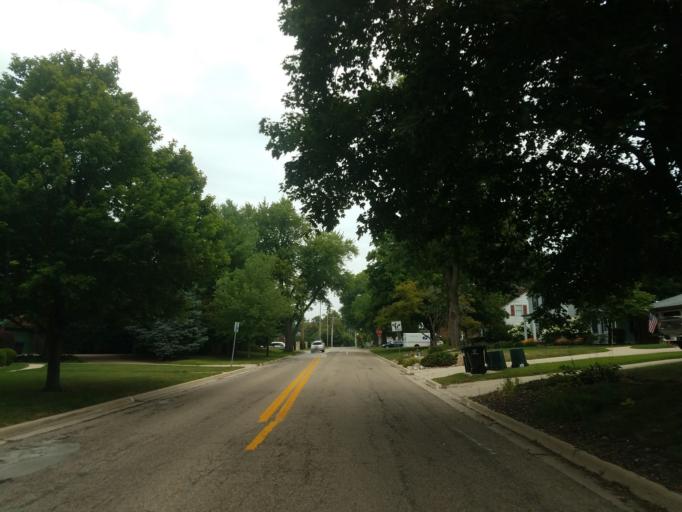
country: US
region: Illinois
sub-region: McLean County
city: Bloomington
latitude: 40.4792
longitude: -88.9627
